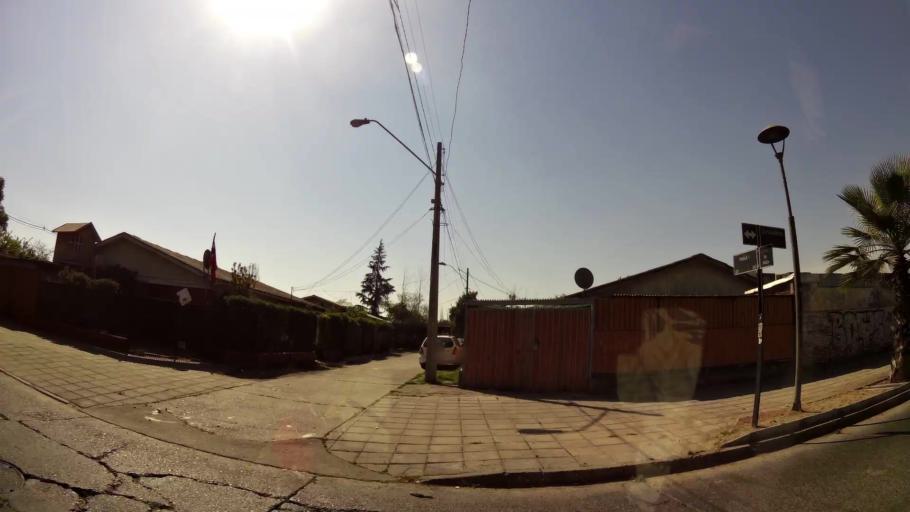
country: CL
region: Santiago Metropolitan
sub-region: Provincia de Santiago
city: La Pintana
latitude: -33.5591
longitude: -70.6300
